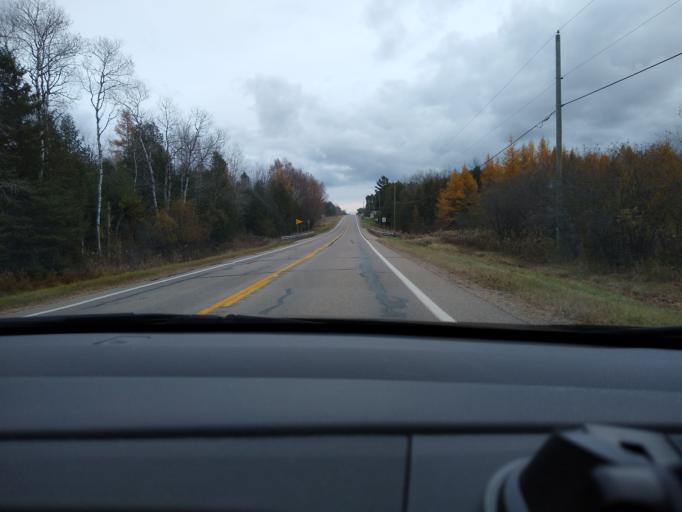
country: US
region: Michigan
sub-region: Delta County
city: Escanaba
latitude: 45.7501
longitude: -87.2823
